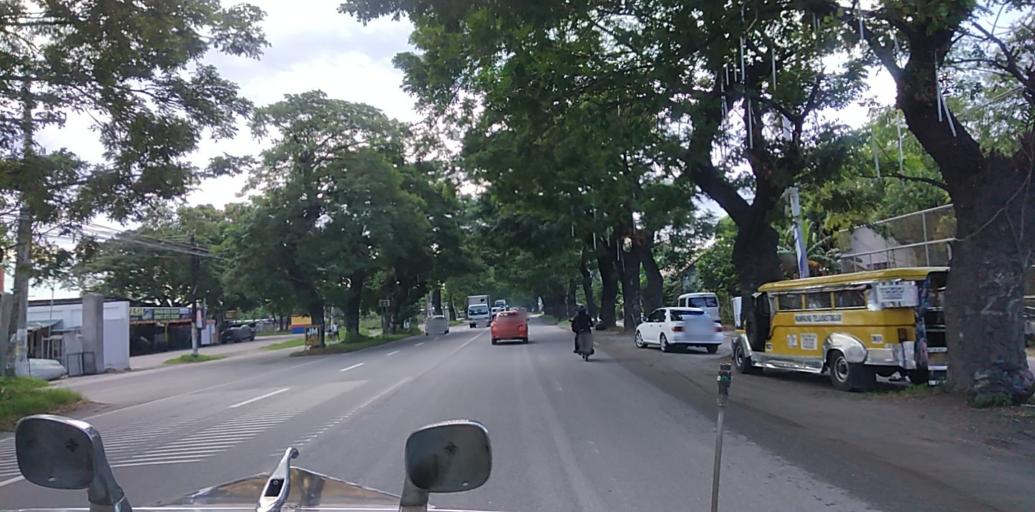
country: PH
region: Central Luzon
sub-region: Province of Pampanga
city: Telabastagan
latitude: 15.1092
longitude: 120.6132
